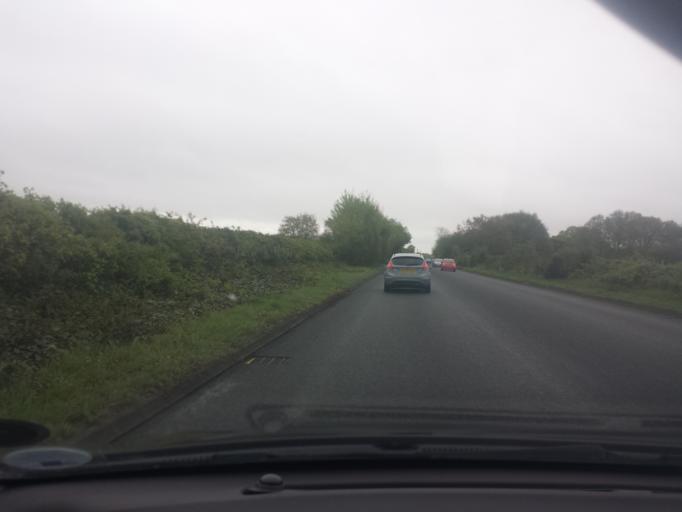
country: GB
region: England
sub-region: Essex
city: Little Clacton
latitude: 51.8309
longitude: 1.1293
